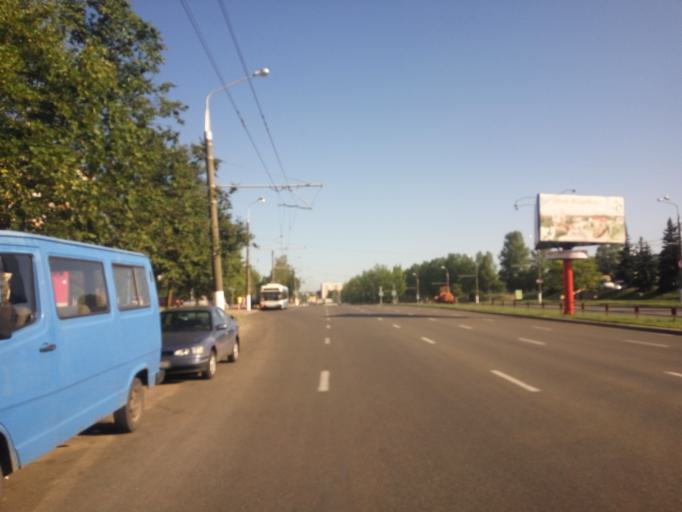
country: BY
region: Vitebsk
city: Vitebsk
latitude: 55.1919
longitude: 30.2498
